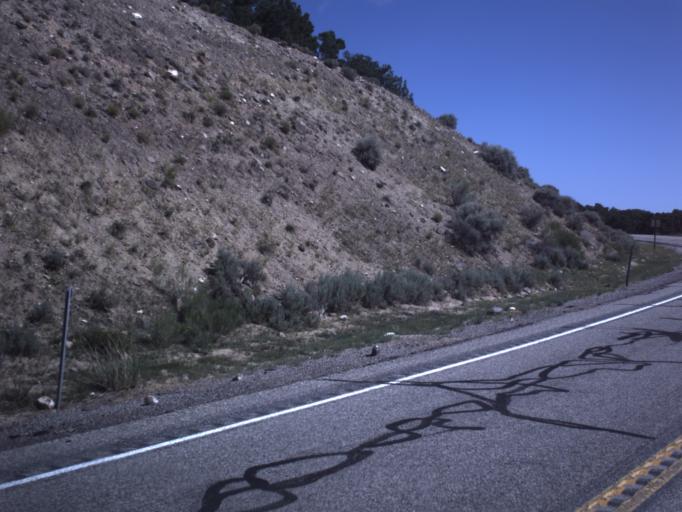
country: US
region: Utah
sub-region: Wayne County
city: Loa
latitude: 38.6922
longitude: -111.3967
